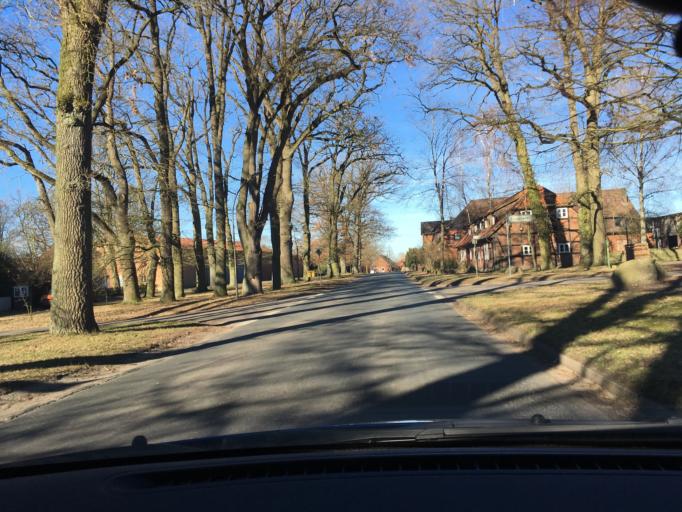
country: DE
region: Lower Saxony
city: Schwienau
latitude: 52.9790
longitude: 10.4452
